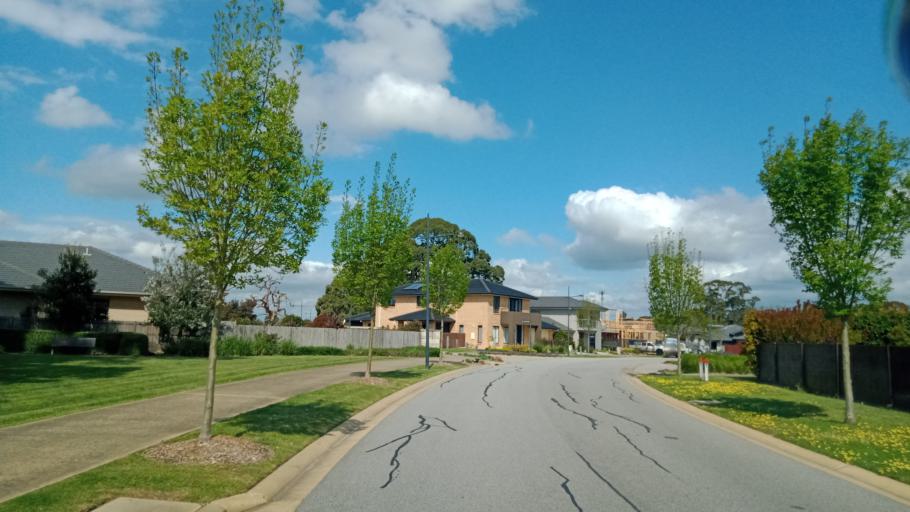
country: AU
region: Victoria
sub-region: Frankston
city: Sandhurst
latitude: -38.0864
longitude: 145.2074
